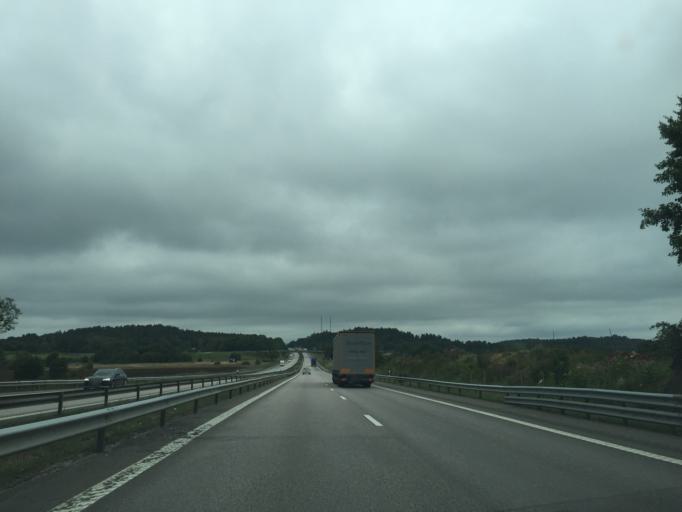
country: SE
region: Halland
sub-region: Kungsbacka Kommun
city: Fjaeras kyrkby
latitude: 57.4141
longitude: 12.1708
